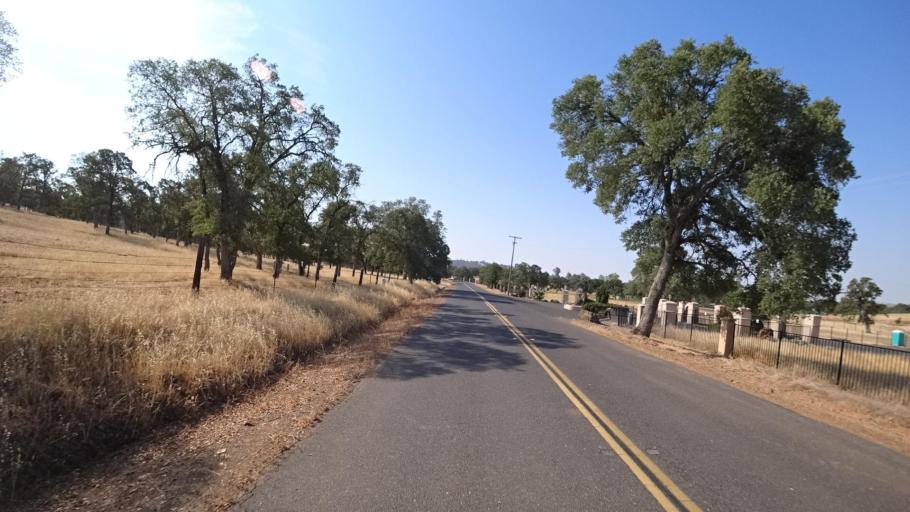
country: US
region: California
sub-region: Tuolumne County
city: Tuolumne City
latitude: 37.7057
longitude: -120.2956
